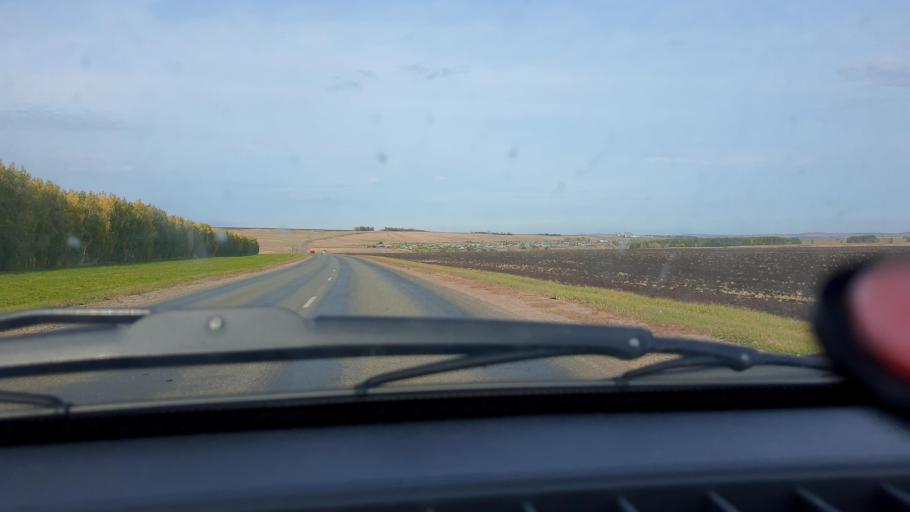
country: RU
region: Bashkortostan
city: Chekmagush
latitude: 54.9807
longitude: 54.5757
